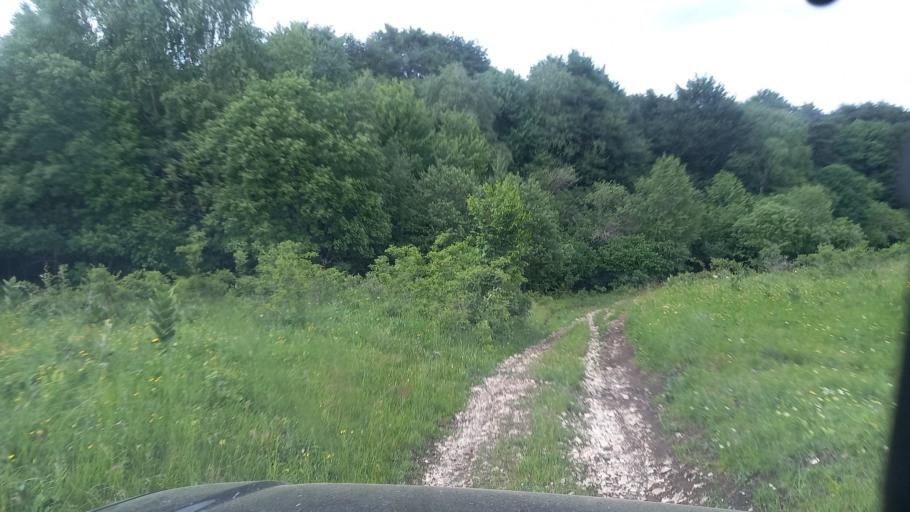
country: RU
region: Karachayevo-Cherkesiya
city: Pregradnaya
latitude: 44.0065
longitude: 41.2784
